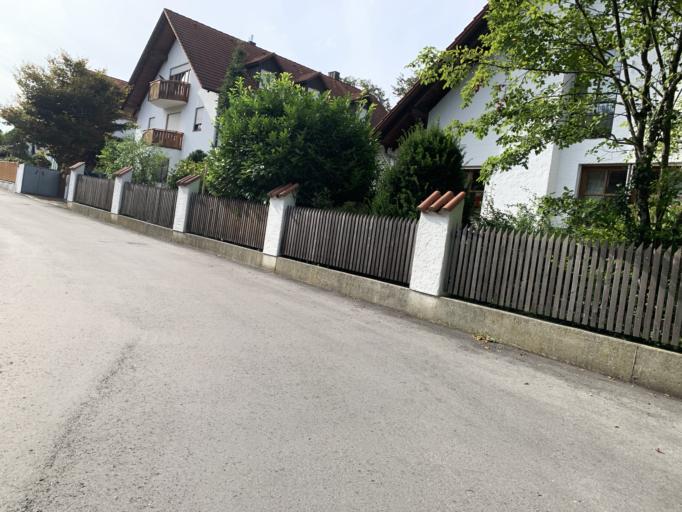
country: DE
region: Bavaria
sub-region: Upper Bavaria
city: Freising
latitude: 48.4146
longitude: 11.7358
